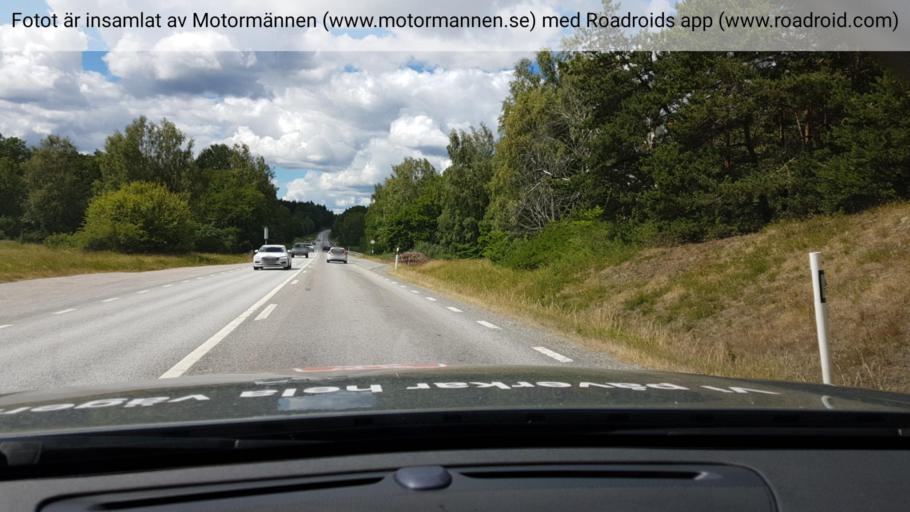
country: SE
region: Stockholm
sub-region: Vaxholms Kommun
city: Resaro
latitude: 59.4226
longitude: 18.2947
